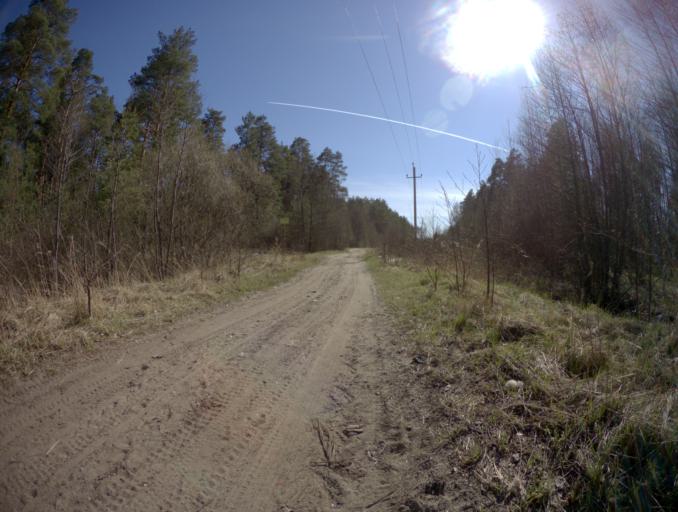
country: RU
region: Vladimir
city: Ivanishchi
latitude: 55.7682
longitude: 40.4170
